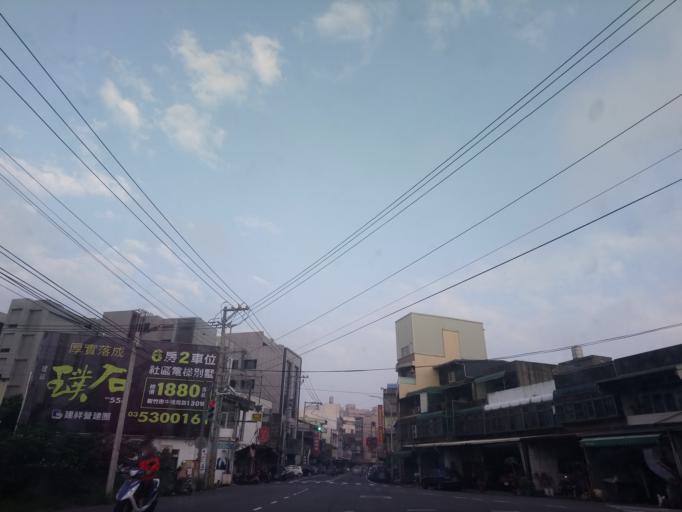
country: TW
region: Taiwan
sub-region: Hsinchu
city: Hsinchu
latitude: 24.7962
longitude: 120.9393
